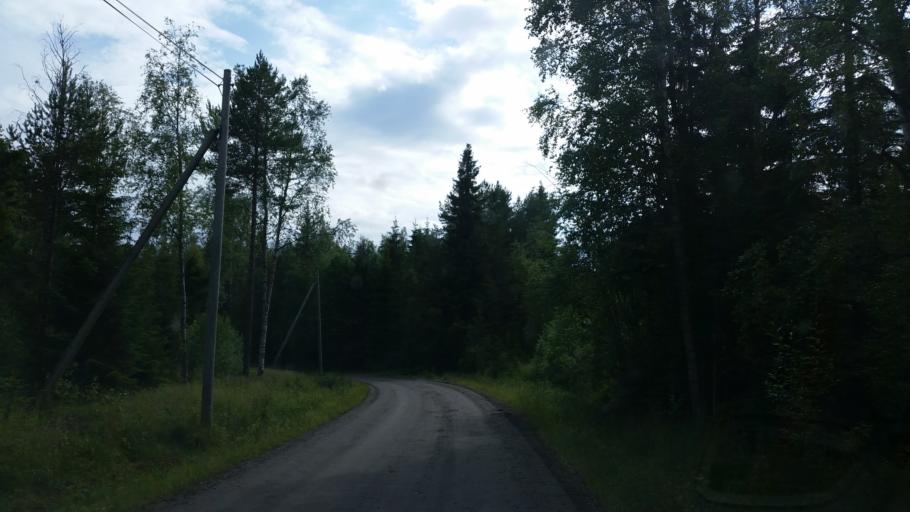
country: SE
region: Vaesterbotten
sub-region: Robertsfors Kommun
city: Robertsfors
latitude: 64.1915
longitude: 21.0443
